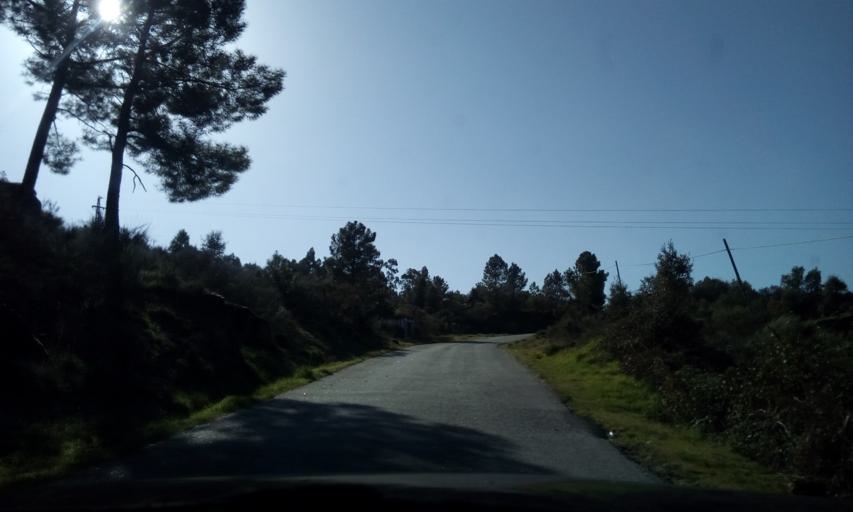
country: PT
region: Guarda
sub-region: Celorico da Beira
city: Celorico da Beira
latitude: 40.6826
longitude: -7.3971
